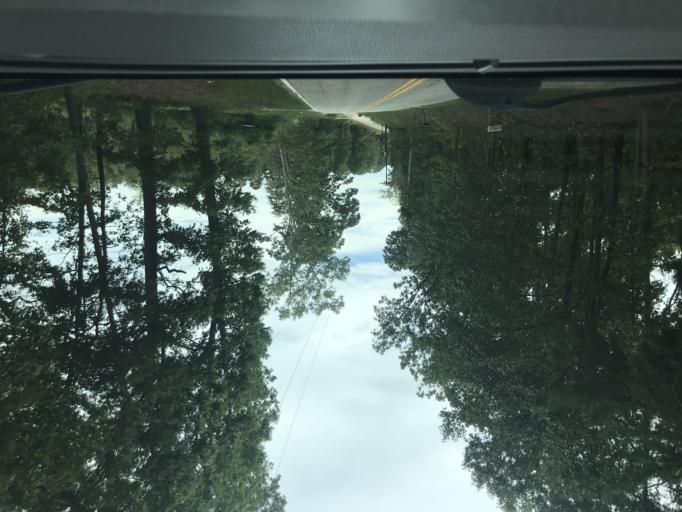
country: US
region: North Carolina
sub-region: Cleveland County
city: Boiling Springs
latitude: 35.1747
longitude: -81.7143
